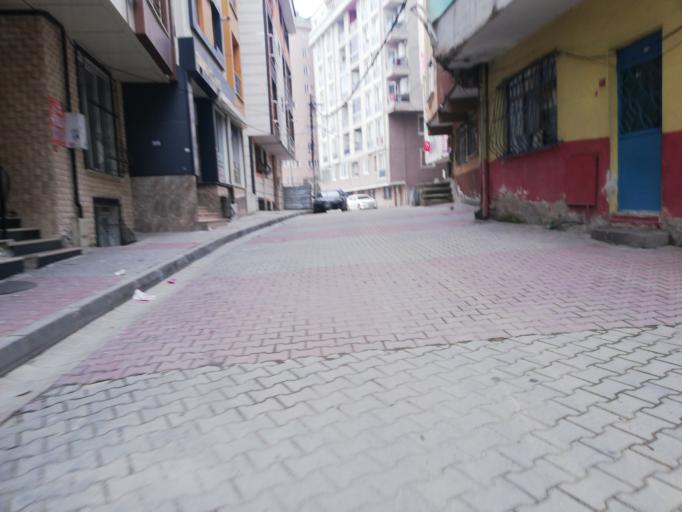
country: TR
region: Istanbul
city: Sisli
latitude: 41.0860
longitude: 28.9722
